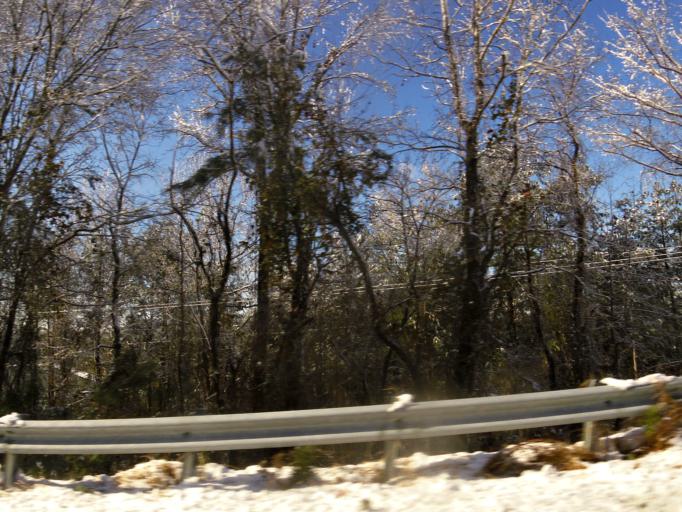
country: US
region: North Carolina
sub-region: Wilson County
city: Elm City
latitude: 35.8200
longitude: -77.8540
